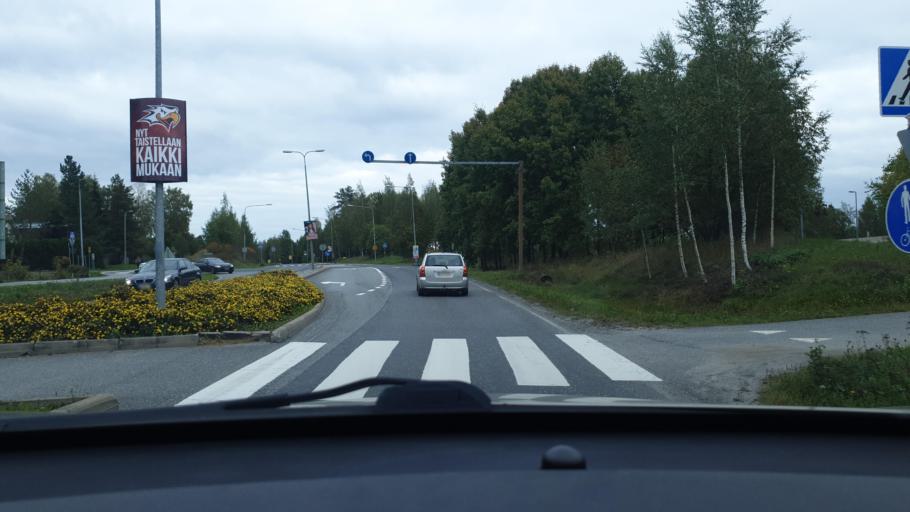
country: FI
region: Ostrobothnia
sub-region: Vaasa
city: Vaasa
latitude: 63.1034
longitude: 21.6411
